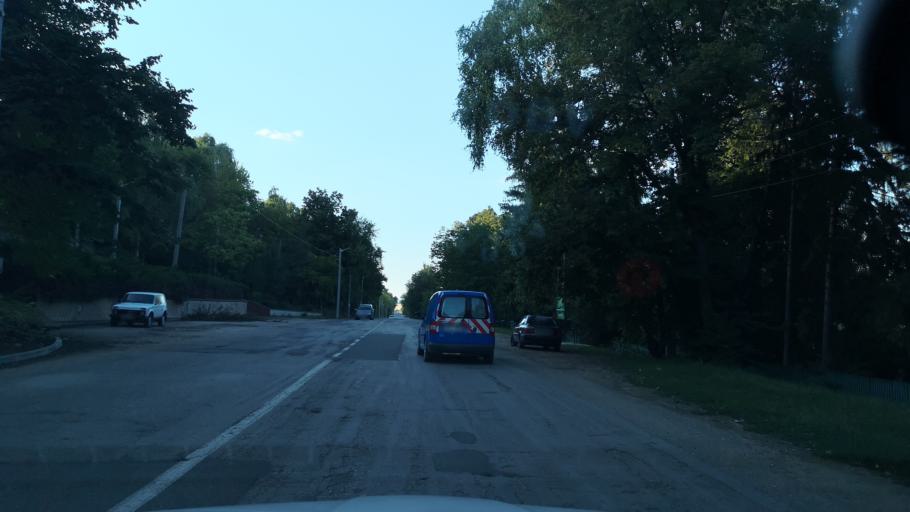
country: MD
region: Orhei
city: Orhei
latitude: 47.3940
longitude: 28.8218
